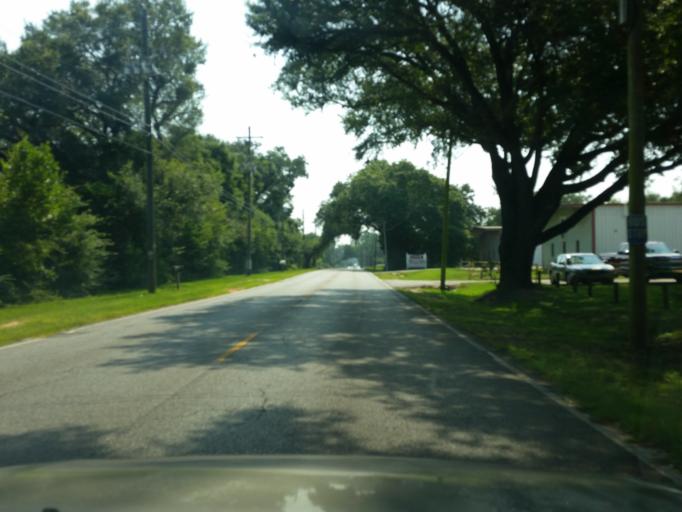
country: US
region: Florida
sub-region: Escambia County
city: Ensley
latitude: 30.5191
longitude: -87.2834
